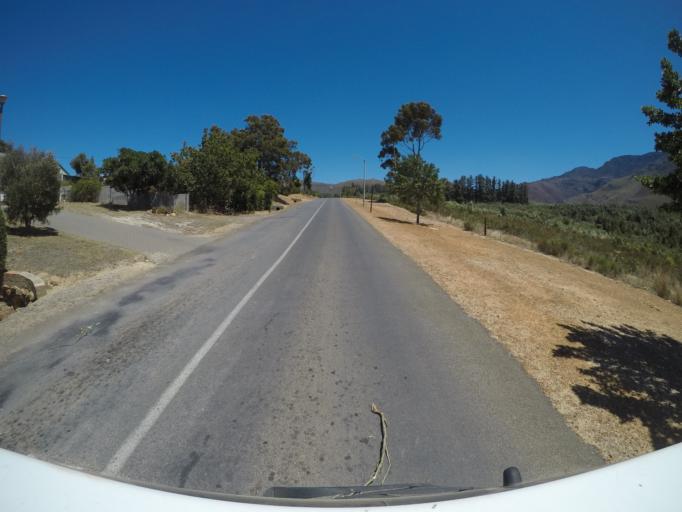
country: ZA
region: Western Cape
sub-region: Overberg District Municipality
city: Hermanus
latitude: -34.2238
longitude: 19.2039
